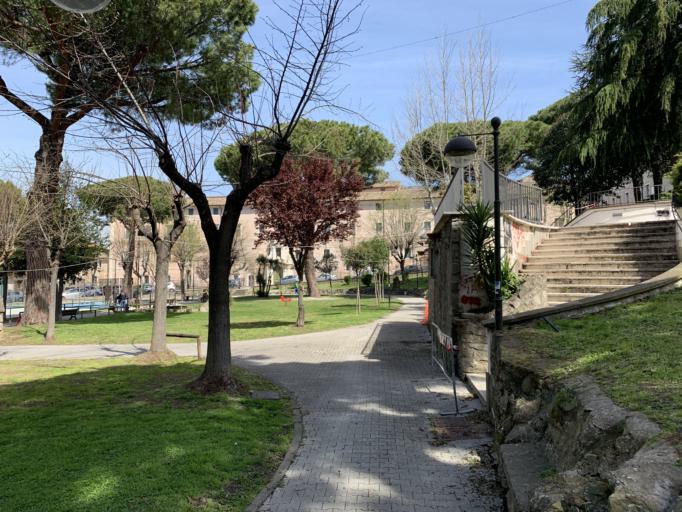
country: IT
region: Latium
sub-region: Citta metropolitana di Roma Capitale
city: Castel Gandolfo
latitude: 41.7704
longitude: 12.6549
